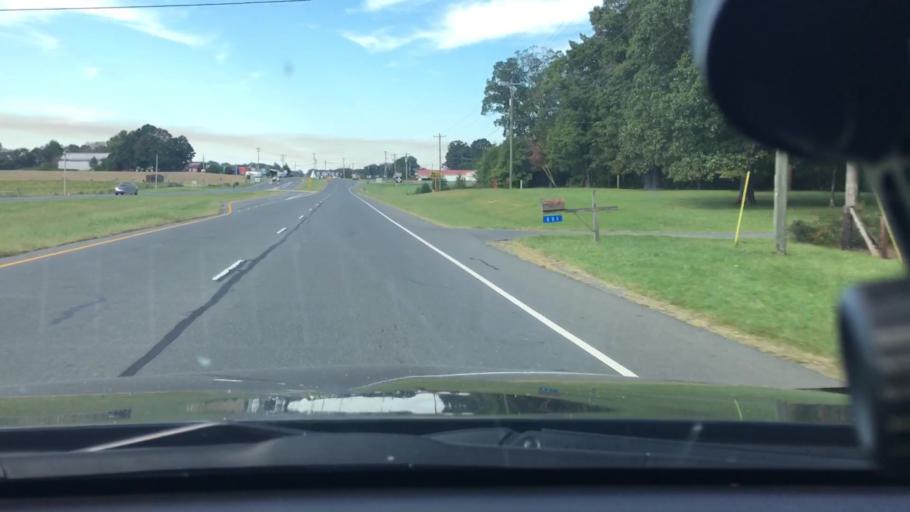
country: US
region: North Carolina
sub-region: Stanly County
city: Oakboro
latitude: 35.2689
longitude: -80.3492
